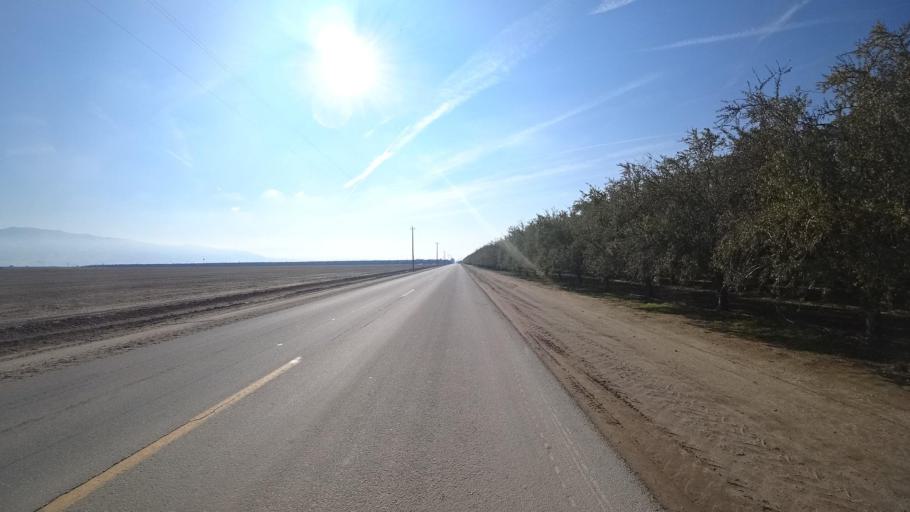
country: US
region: California
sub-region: Kern County
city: Arvin
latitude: 35.2435
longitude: -118.8605
